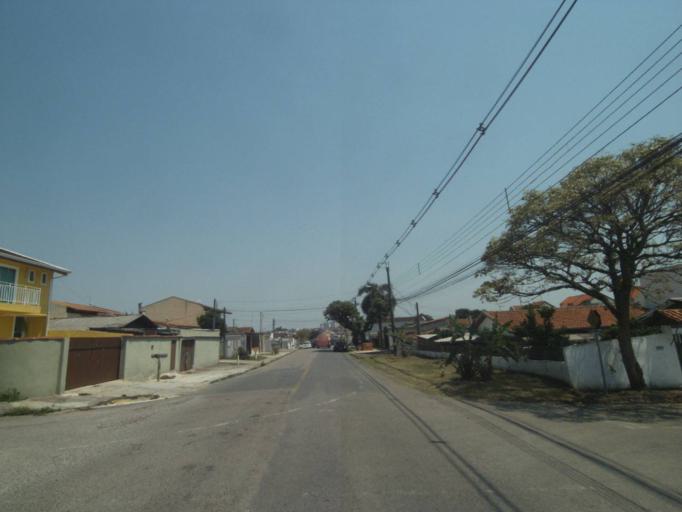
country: BR
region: Parana
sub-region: Sao Jose Dos Pinhais
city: Sao Jose dos Pinhais
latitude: -25.5111
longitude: -49.2682
